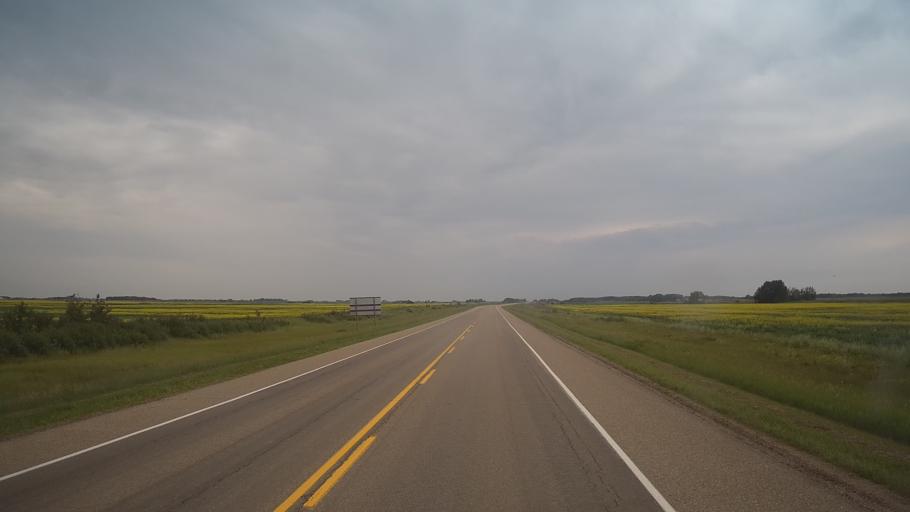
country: CA
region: Saskatchewan
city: Langham
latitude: 52.1282
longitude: -107.2429
